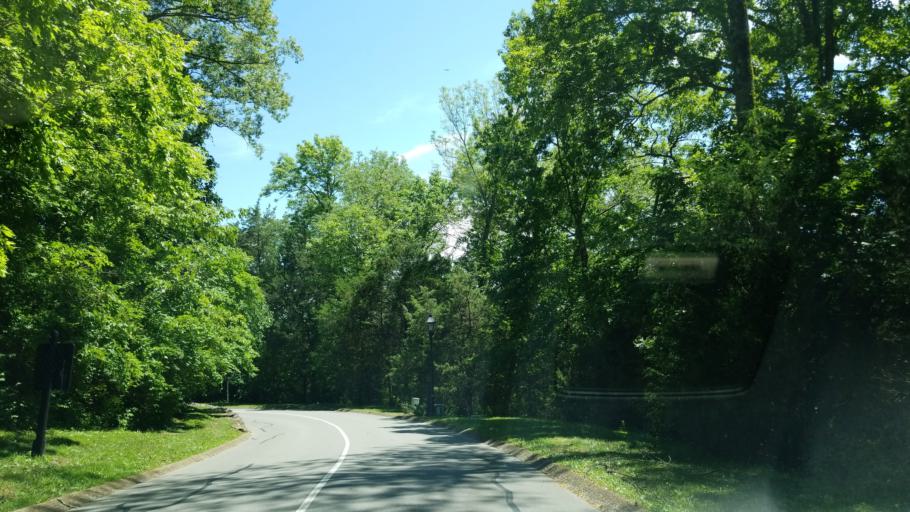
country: US
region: Tennessee
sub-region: Davidson County
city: Forest Hills
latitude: 36.0518
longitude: -86.8215
